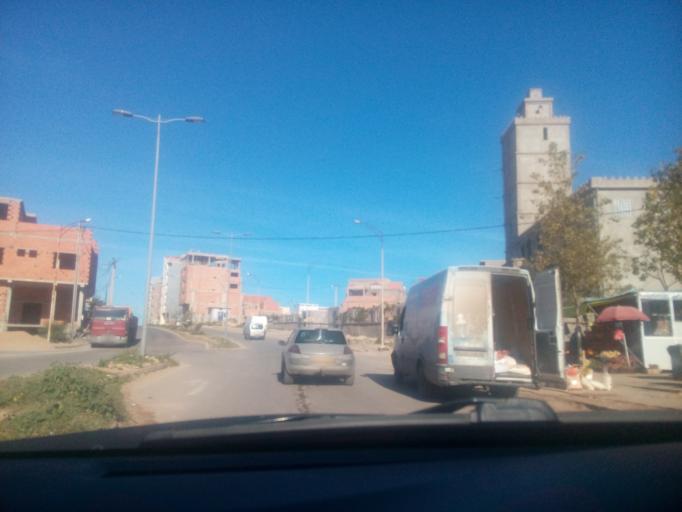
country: DZ
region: Oran
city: Bir el Djir
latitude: 35.7483
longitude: -0.5504
